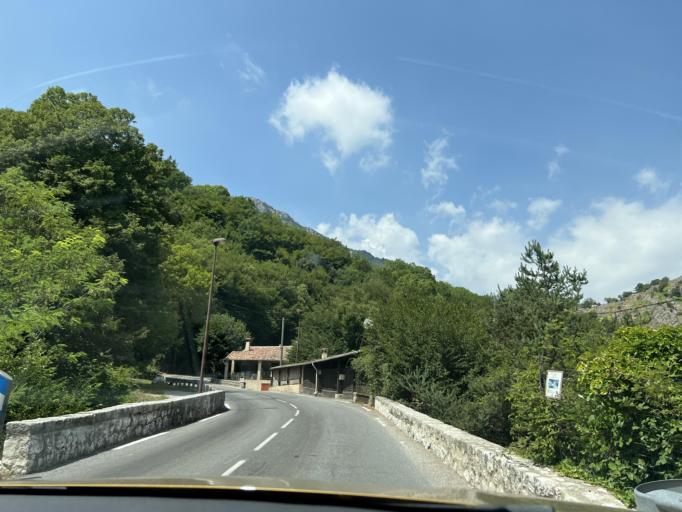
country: FR
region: Provence-Alpes-Cote d'Azur
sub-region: Departement des Alpes-Maritimes
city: Tourrettes-sur-Loup
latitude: 43.7478
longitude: 6.9977
